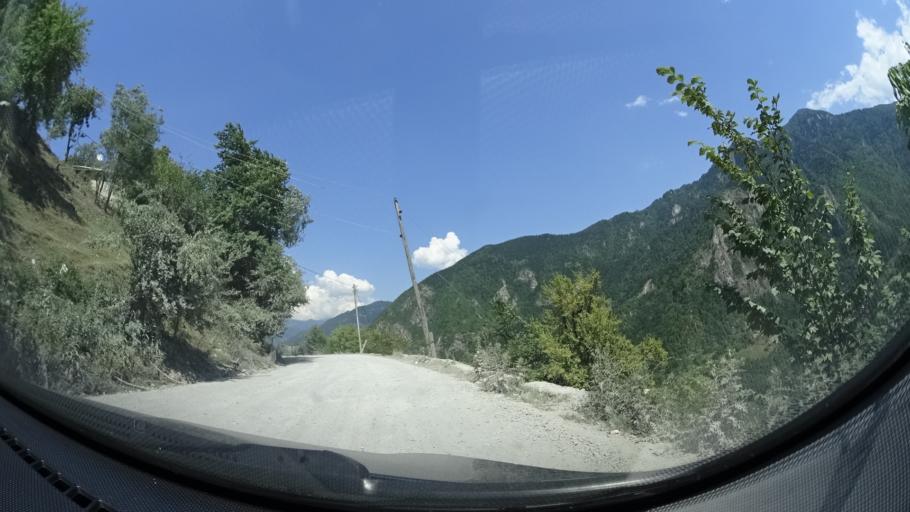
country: GE
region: Ajaria
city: Khulo
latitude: 41.6437
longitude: 42.3161
